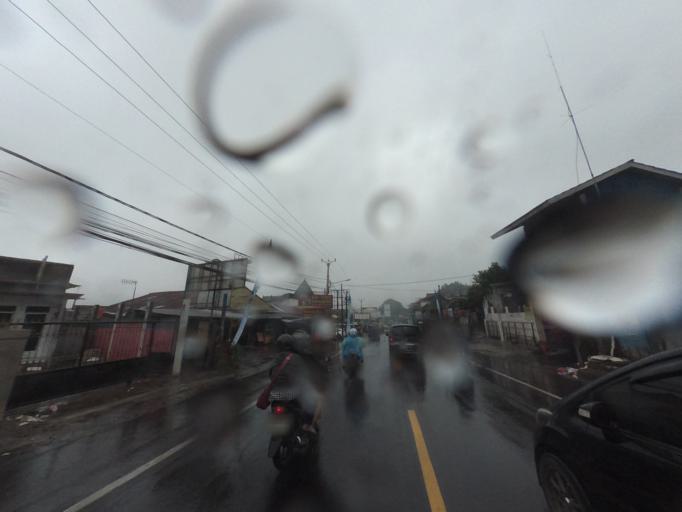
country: ID
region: West Java
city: Caringin
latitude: -6.6548
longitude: 106.8621
